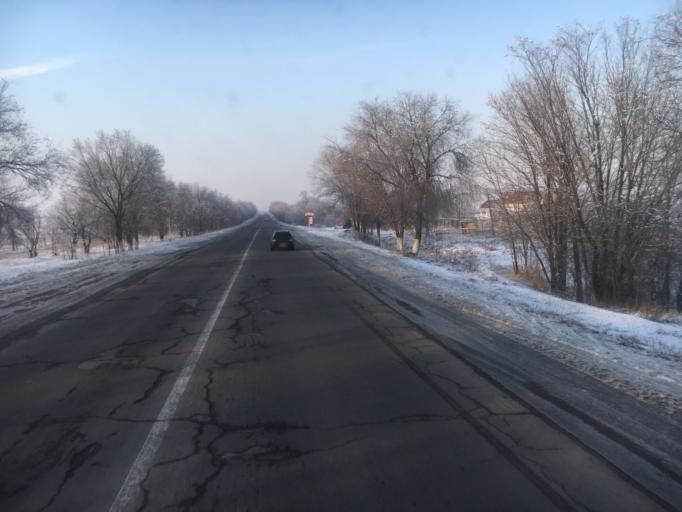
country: KZ
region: Almaty Oblysy
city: Burunday
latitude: 43.3100
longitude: 76.6662
